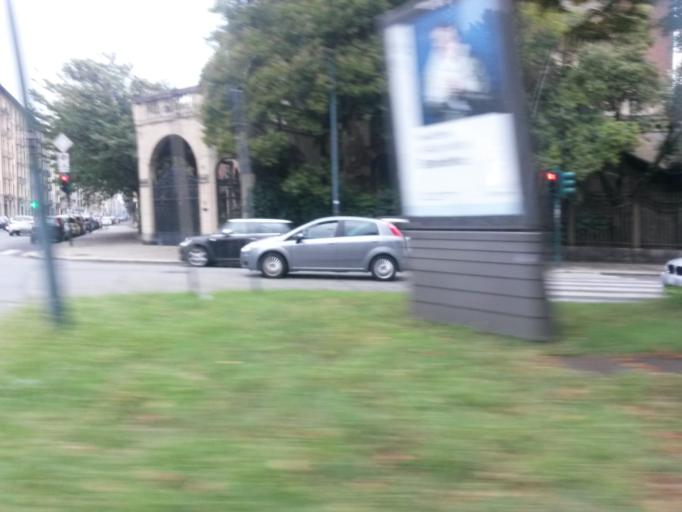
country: IT
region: Piedmont
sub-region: Provincia di Torino
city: Turin
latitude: 45.0833
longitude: 7.6486
